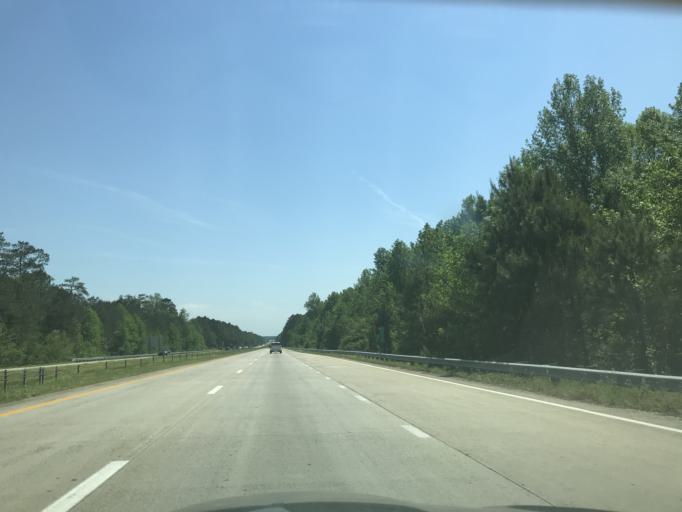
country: US
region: North Carolina
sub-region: Johnston County
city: Benson
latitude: 35.5118
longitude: -78.5561
